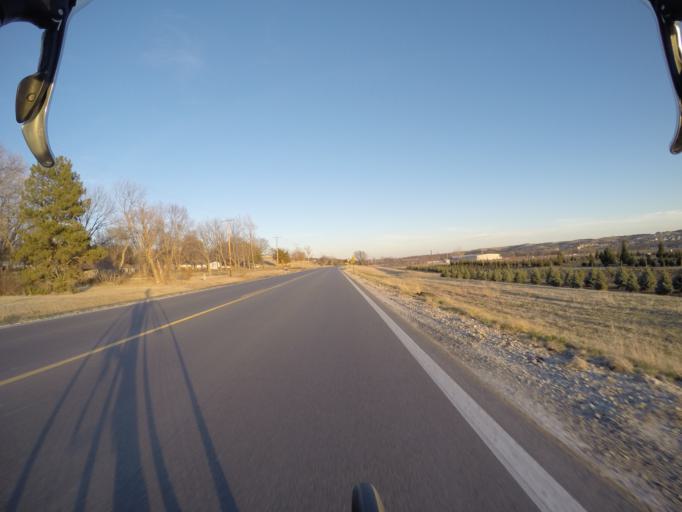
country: US
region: Kansas
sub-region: Riley County
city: Manhattan
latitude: 39.1958
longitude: -96.6476
